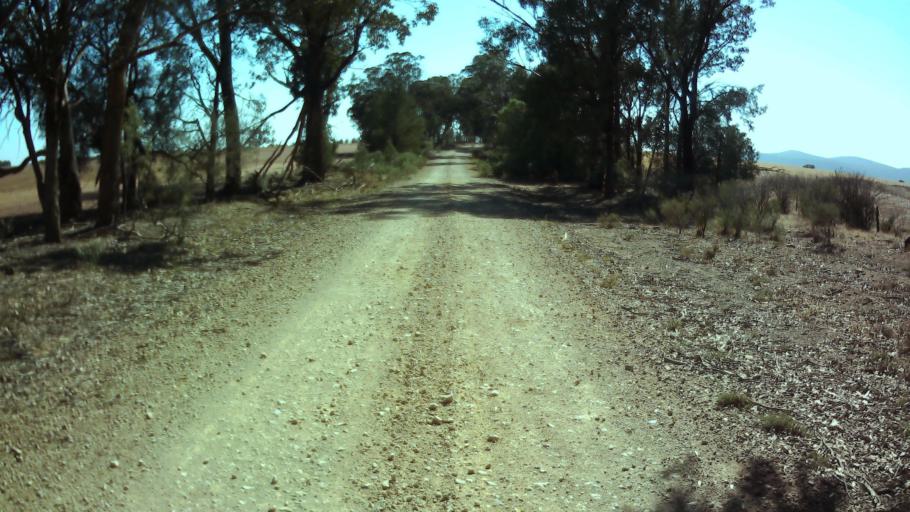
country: AU
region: New South Wales
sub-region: Weddin
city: Grenfell
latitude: -33.9068
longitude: 147.8533
